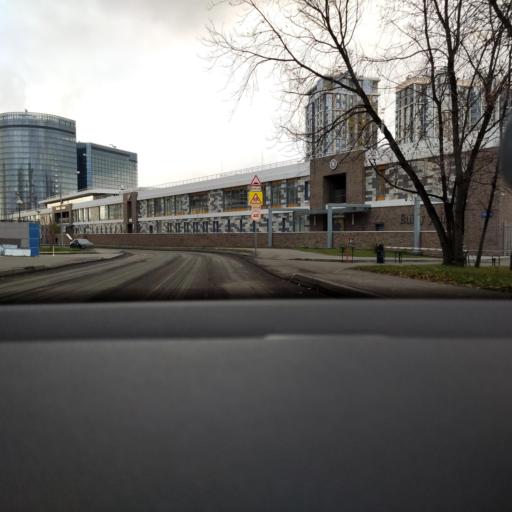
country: RU
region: Moscow
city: Sviblovo
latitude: 55.8492
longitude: 37.6341
